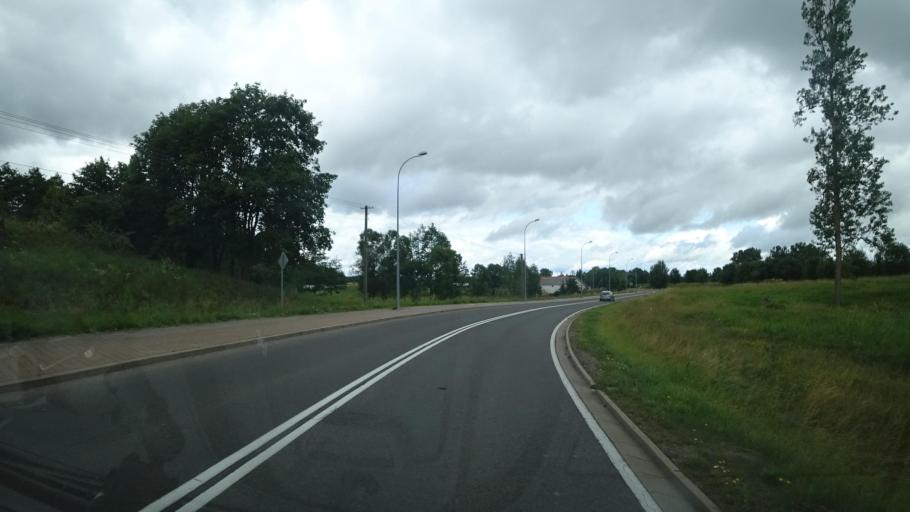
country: PL
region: Warmian-Masurian Voivodeship
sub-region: Powiat olecki
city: Kowale Oleckie
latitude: 54.1760
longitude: 22.4139
